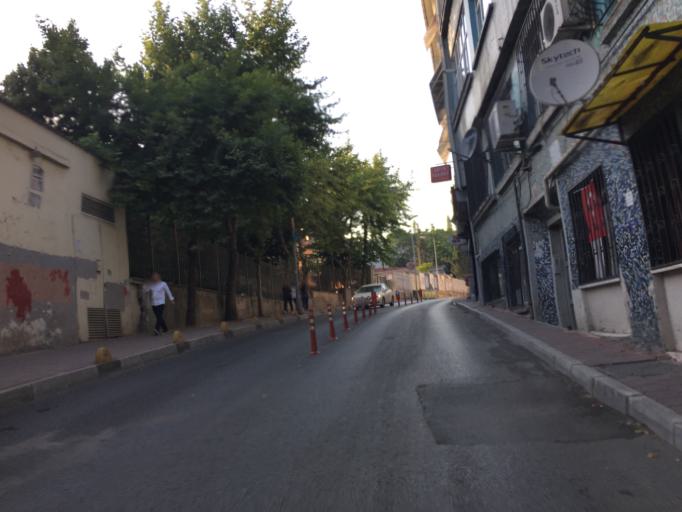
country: TR
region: Istanbul
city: Istanbul
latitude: 41.0058
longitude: 28.9426
